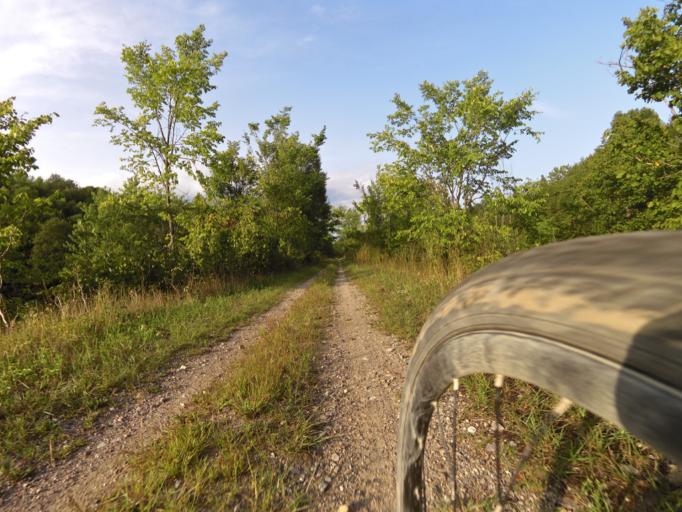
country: CA
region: Ontario
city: Kingston
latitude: 44.5220
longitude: -76.4132
